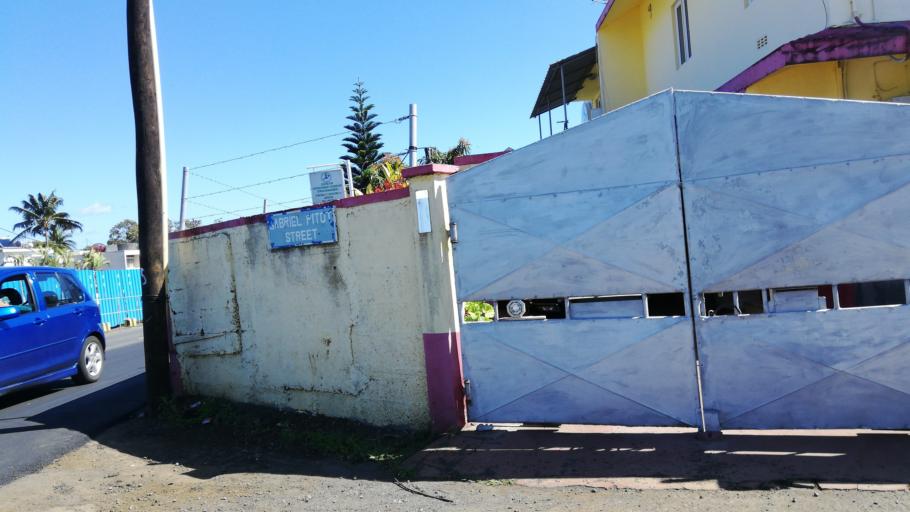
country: MU
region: Plaines Wilhems
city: Ebene
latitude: -20.2363
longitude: 57.4742
